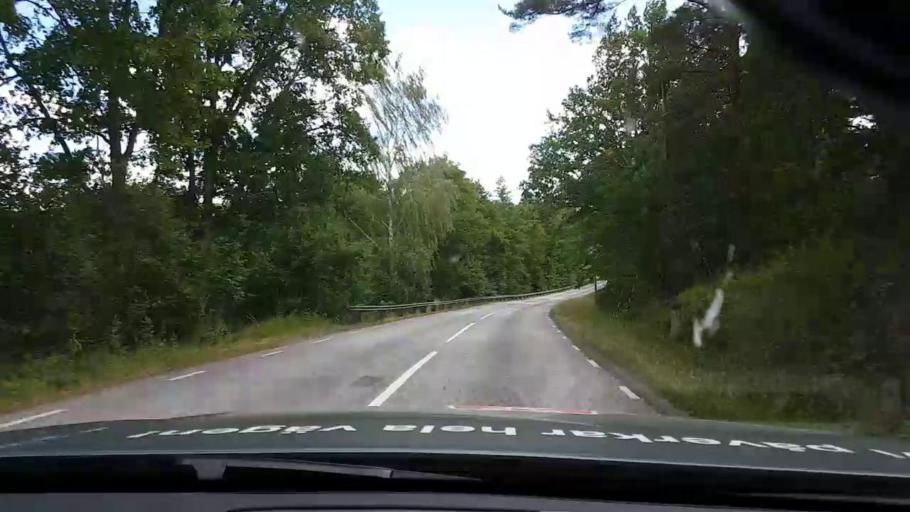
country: SE
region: Kalmar
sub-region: Vasterviks Kommun
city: Forserum
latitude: 58.0371
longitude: 16.4451
